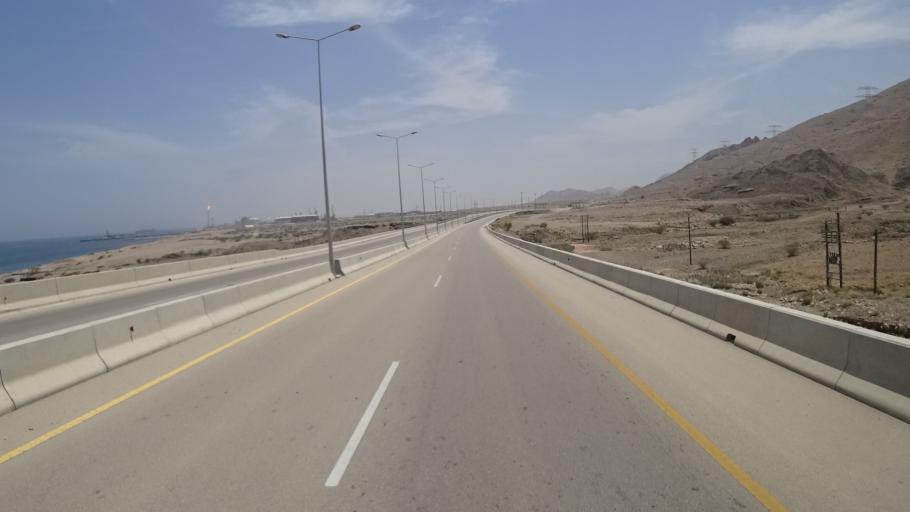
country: OM
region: Ash Sharqiyah
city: Sur
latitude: 22.6750
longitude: 59.3863
